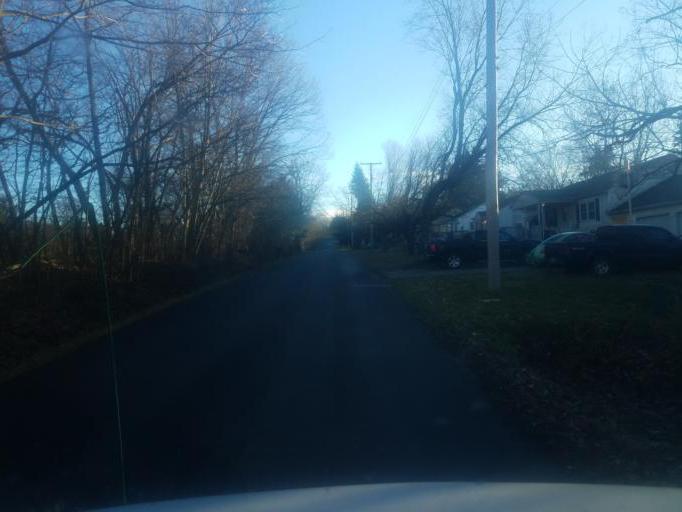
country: US
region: Ohio
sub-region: Richland County
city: Mansfield
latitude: 40.7869
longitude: -82.5425
